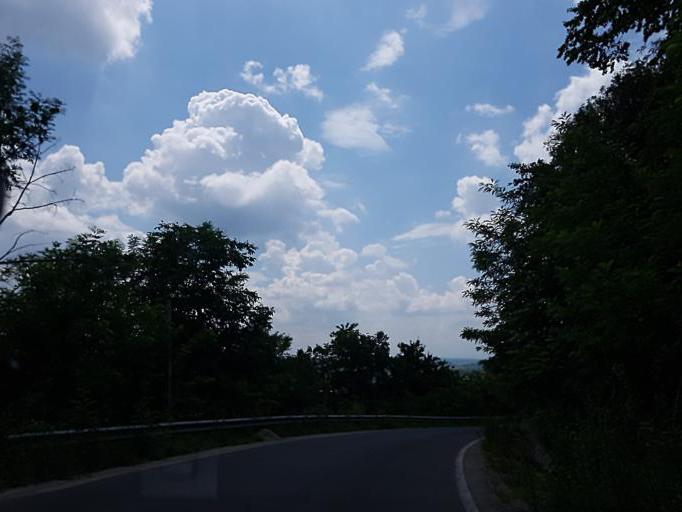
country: RO
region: Sibiu
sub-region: Comuna Seica Mare
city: Seica Mare
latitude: 46.0346
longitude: 24.1606
